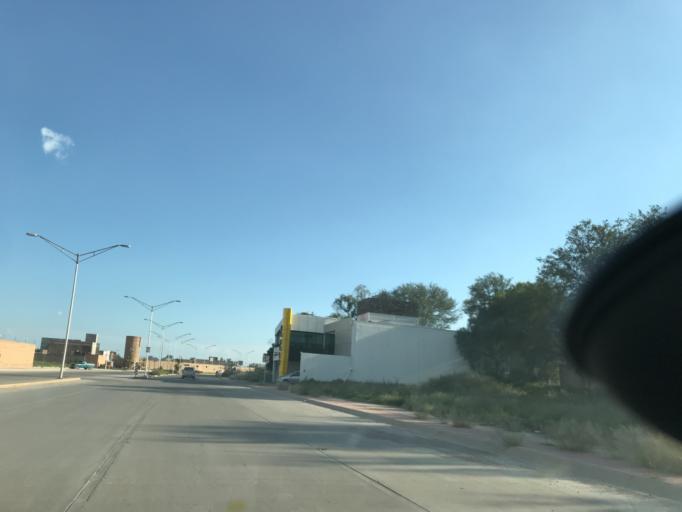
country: MX
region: Aguascalientes
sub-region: Aguascalientes
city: Pocitos
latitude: 21.9049
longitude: -102.3304
